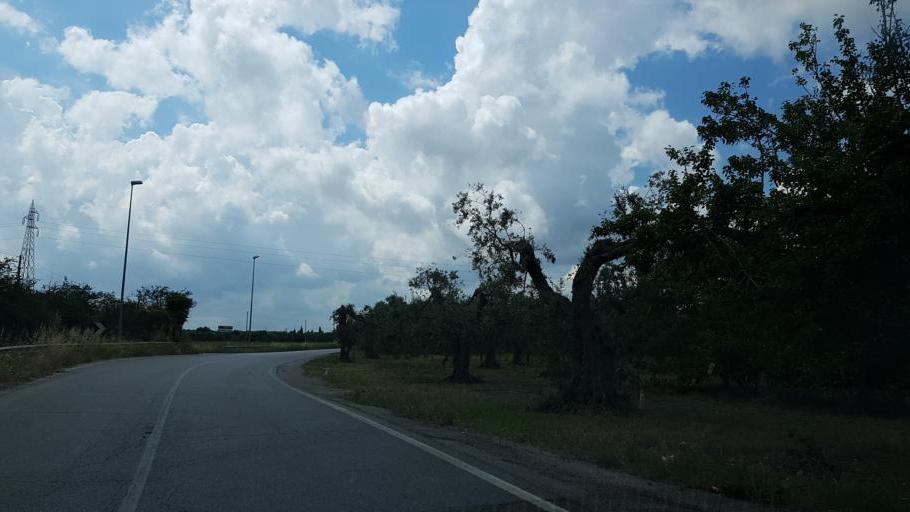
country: IT
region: Apulia
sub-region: Provincia di Brindisi
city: Mesagne
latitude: 40.5387
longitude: 17.8175
